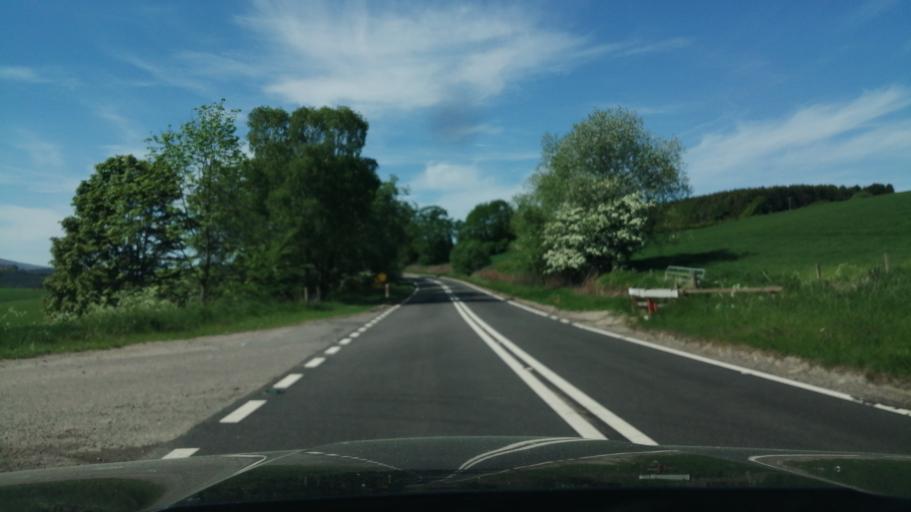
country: GB
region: Scotland
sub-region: Moray
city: Dufftown
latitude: 57.4937
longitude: -3.1516
